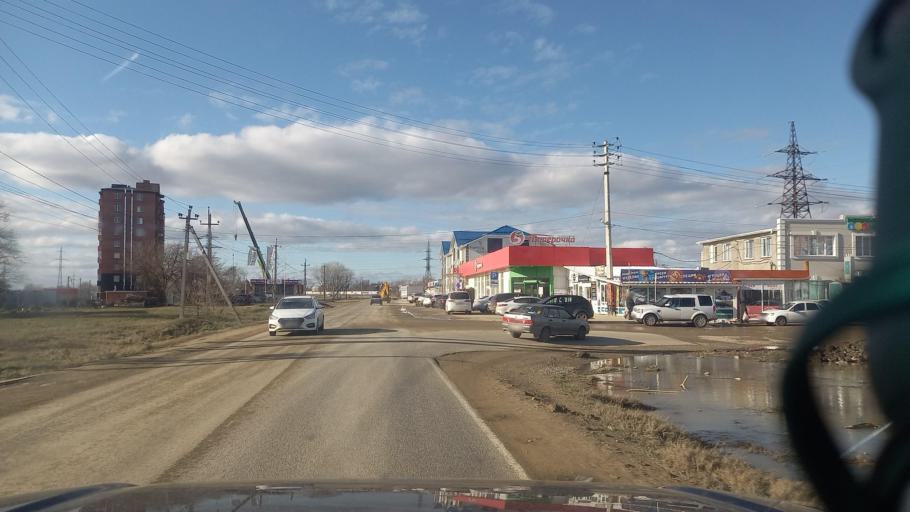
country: RU
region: Adygeya
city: Yablonovskiy
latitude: 45.0156
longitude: 38.9136
